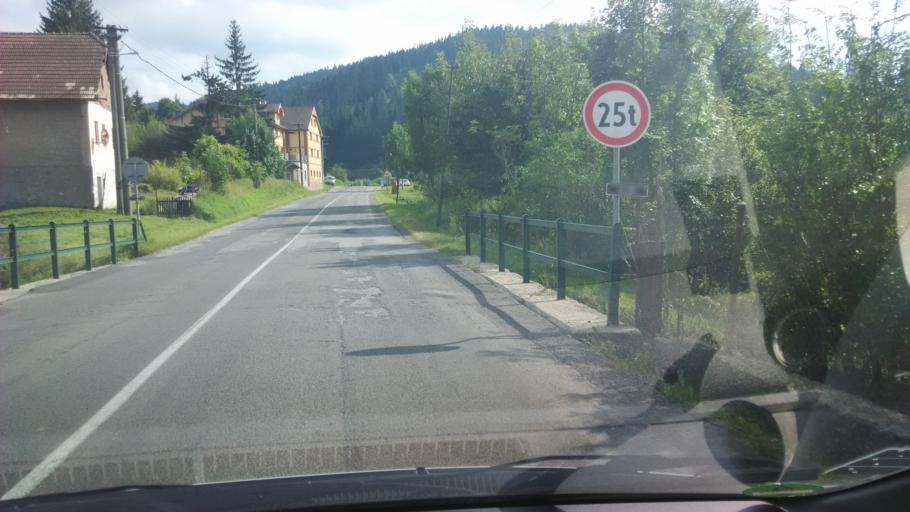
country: SK
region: Banskobystricky
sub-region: Okres Ziar nad Hronom
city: Kremnica
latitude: 48.7658
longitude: 18.9052
